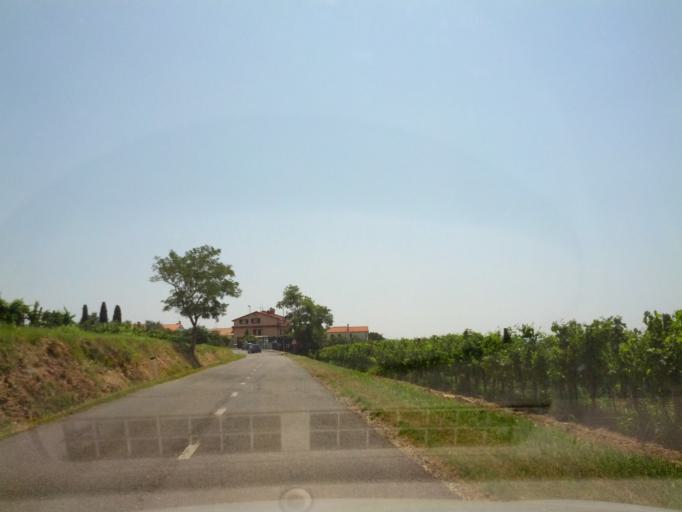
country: SI
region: Koper-Capodistria
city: Ankaran
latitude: 45.5870
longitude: 13.7138
